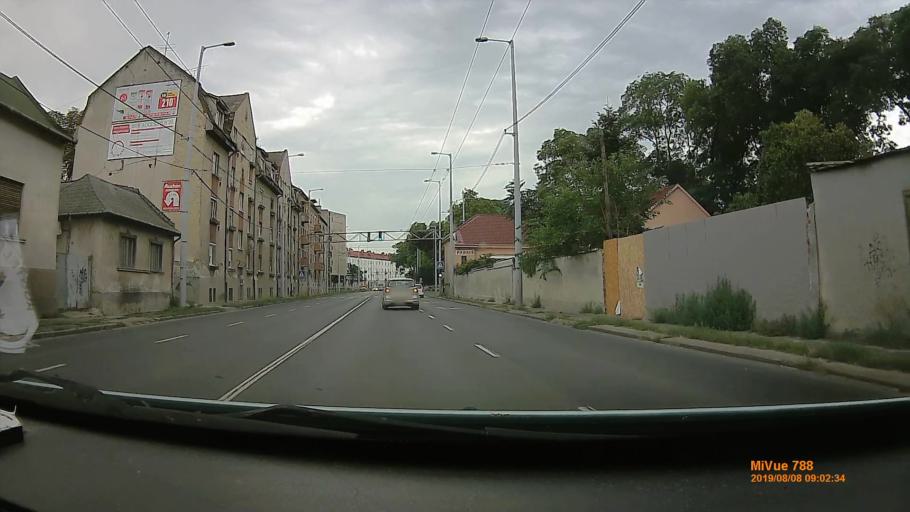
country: HU
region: Hajdu-Bihar
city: Debrecen
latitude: 47.5344
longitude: 21.6392
